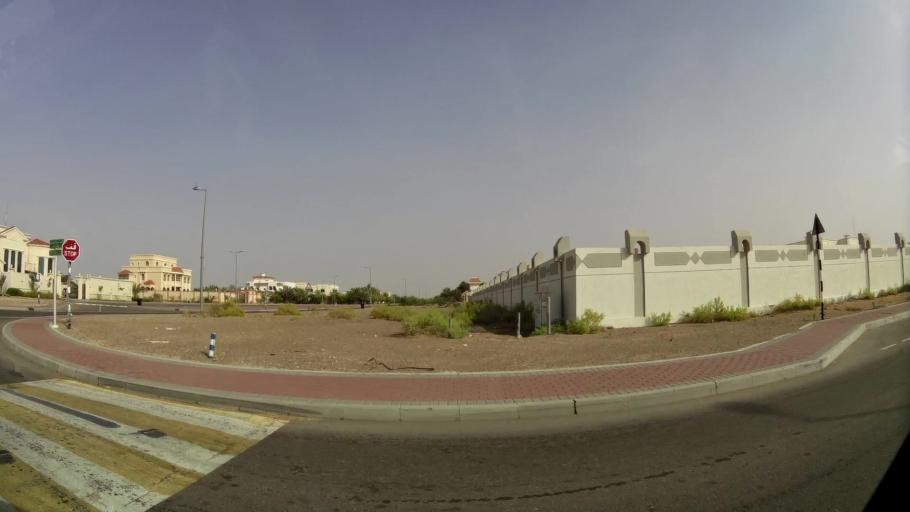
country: AE
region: Abu Dhabi
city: Al Ain
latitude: 24.1983
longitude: 55.6160
